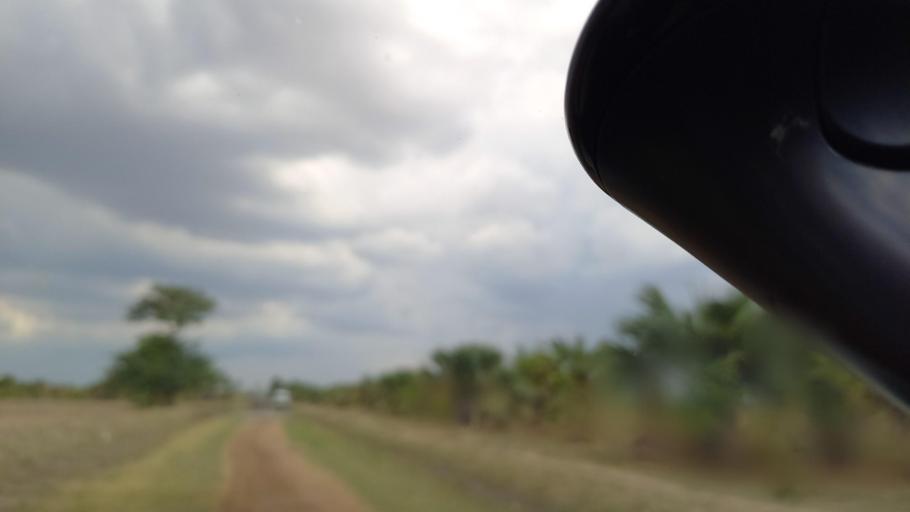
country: ZM
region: Lusaka
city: Kafue
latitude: -15.8351
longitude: 28.0755
